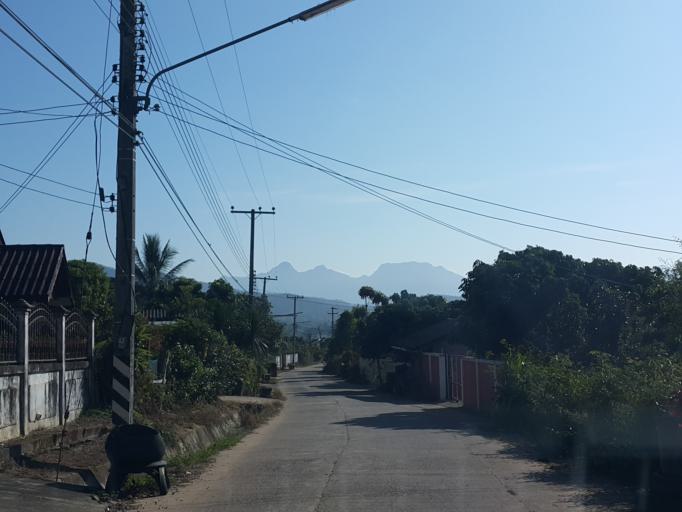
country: TH
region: Chiang Mai
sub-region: Amphoe Chiang Dao
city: Chiang Dao
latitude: 19.4686
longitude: 98.9530
